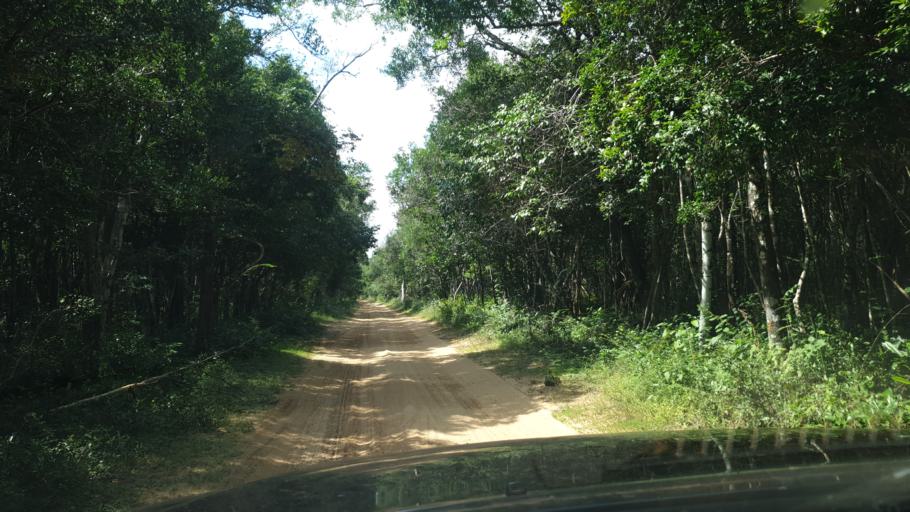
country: LK
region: North Central
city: Anuradhapura
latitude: 8.4183
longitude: 80.0202
